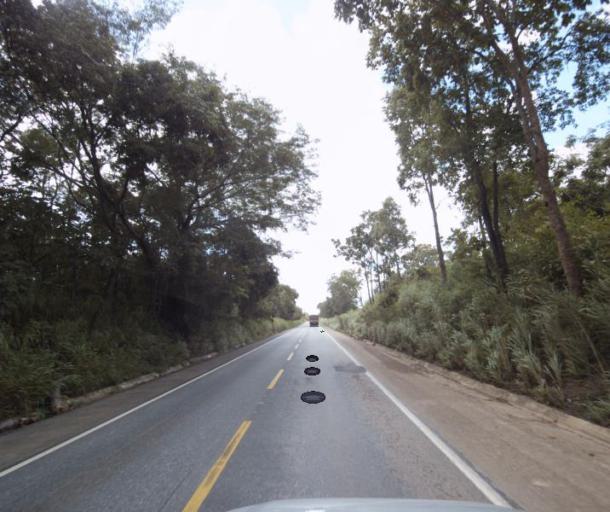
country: BR
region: Goias
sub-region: Porangatu
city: Porangatu
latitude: -13.3010
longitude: -49.1211
